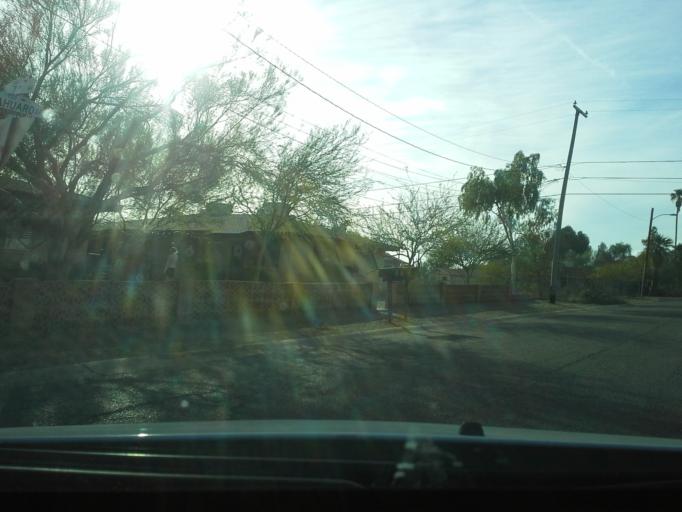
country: US
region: Arizona
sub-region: Maricopa County
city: Glendale
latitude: 33.5841
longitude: -112.0824
